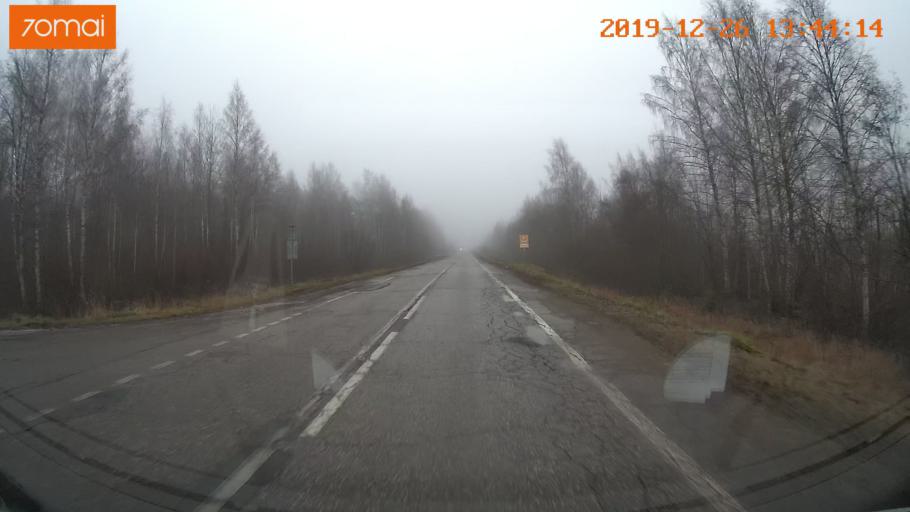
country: RU
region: Vologda
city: Sheksna
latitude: 58.7035
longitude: 38.5038
